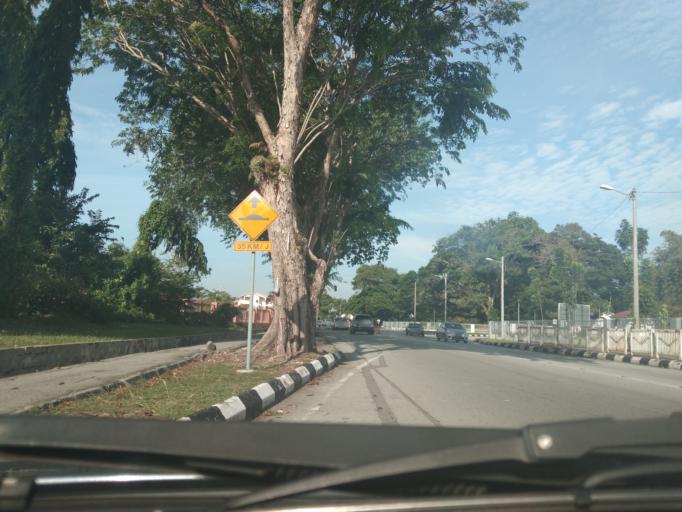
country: MY
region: Perak
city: Ipoh
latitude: 4.5939
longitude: 101.1241
